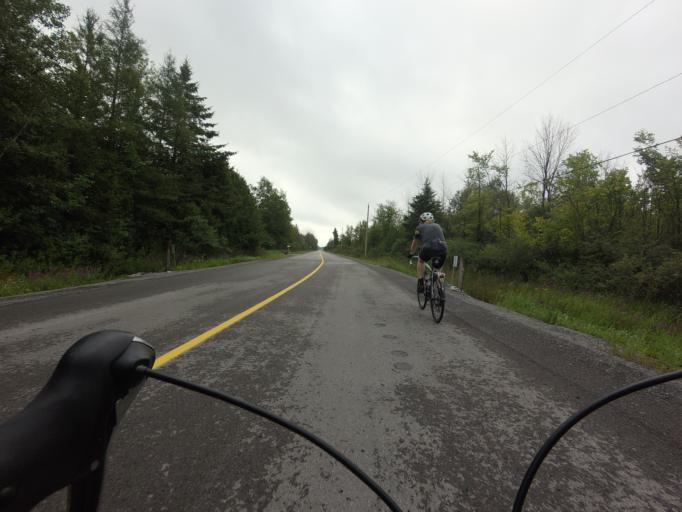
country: CA
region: Ontario
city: Bells Corners
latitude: 45.0791
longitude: -75.7431
